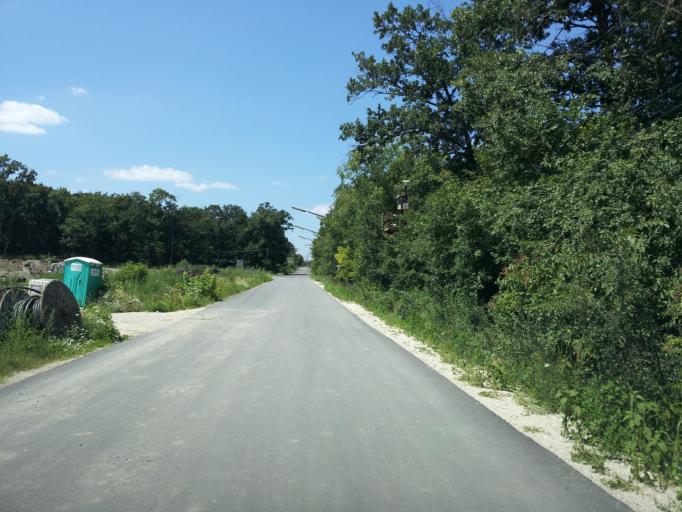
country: HU
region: Veszprem
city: Berhida
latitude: 47.1216
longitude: 18.1014
